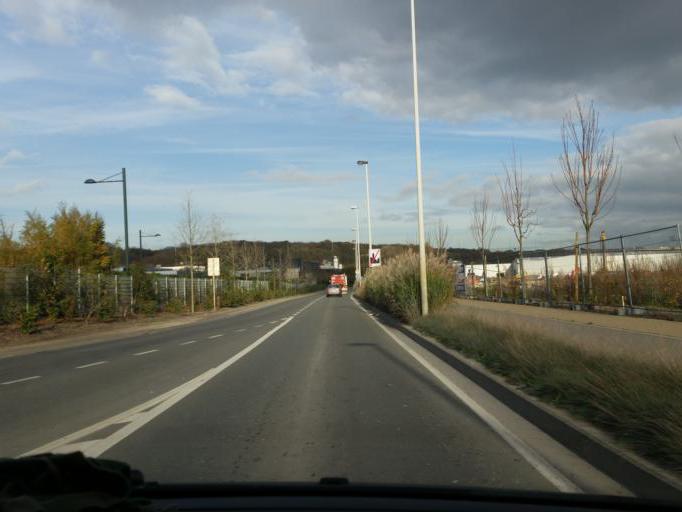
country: BE
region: Flanders
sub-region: Provincie Vlaams-Brabant
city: Diegem
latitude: 50.9058
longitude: 4.4049
